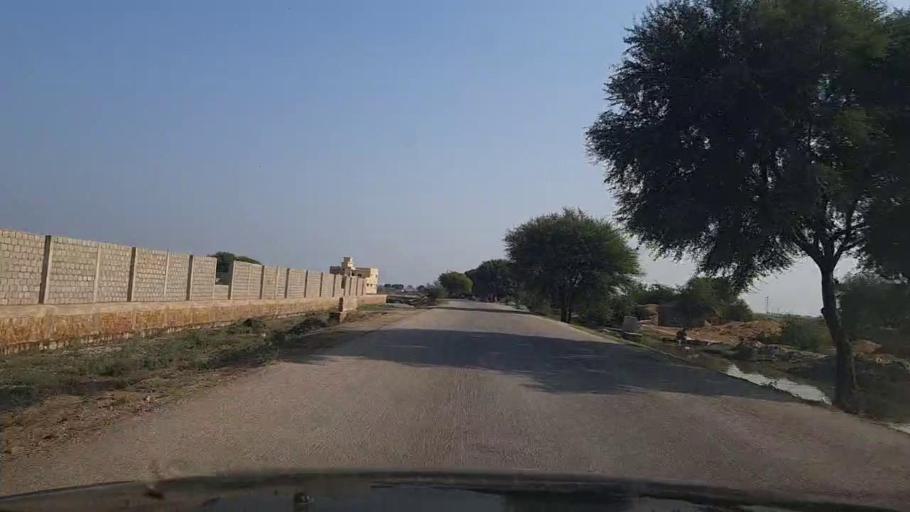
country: PK
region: Sindh
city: Chuhar Jamali
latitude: 24.5893
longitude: 68.0807
